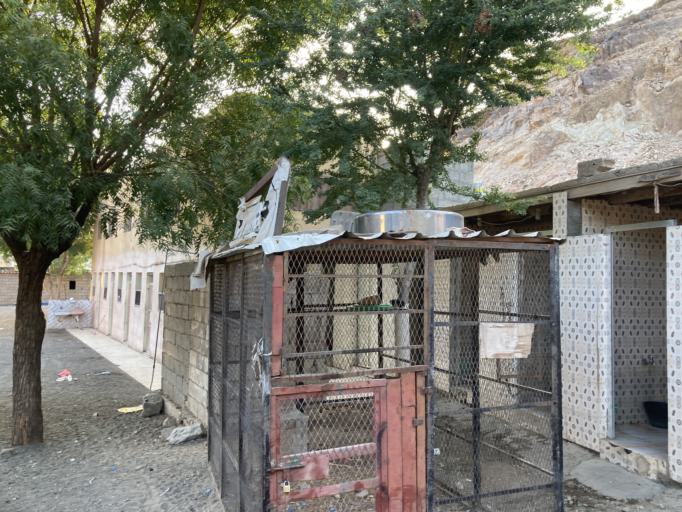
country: YE
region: Lahij
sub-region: Al Milah
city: Al Milah
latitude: 13.3603
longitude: 44.7738
